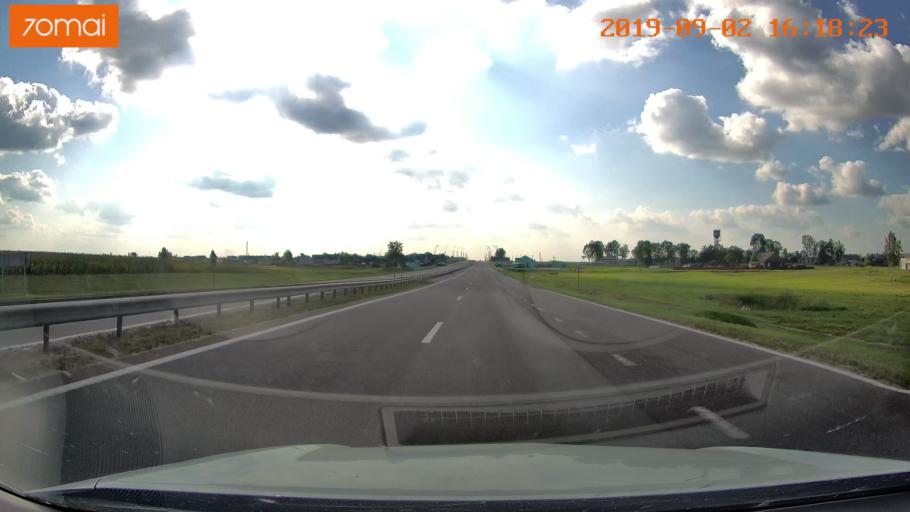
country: BY
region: Minsk
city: Chervyen'
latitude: 53.7293
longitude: 28.4417
